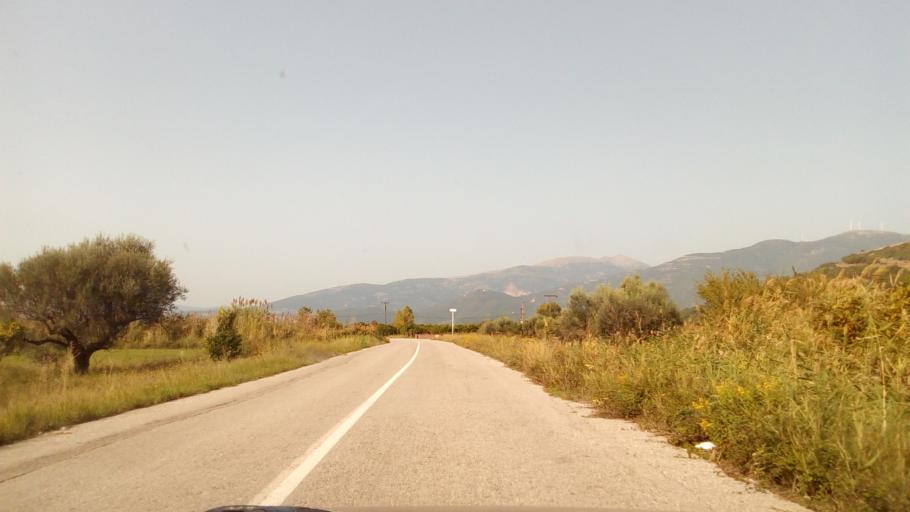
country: GR
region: West Greece
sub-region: Nomos Aitolias kai Akarnanias
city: Nafpaktos
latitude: 38.4037
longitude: 21.9140
